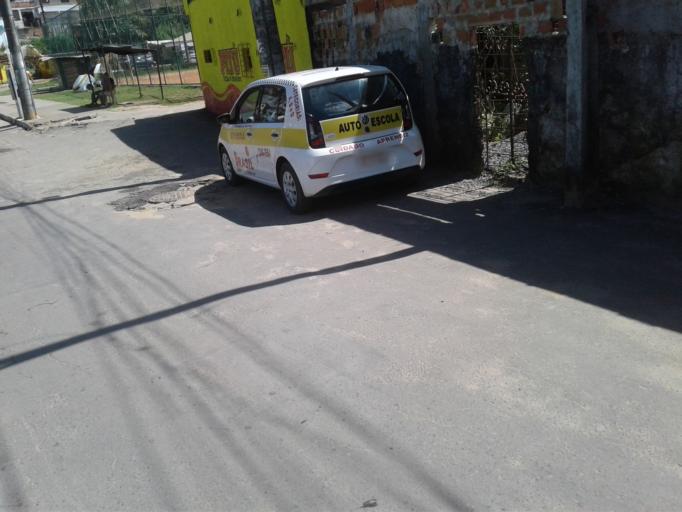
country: BR
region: Bahia
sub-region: Salvador
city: Salvador
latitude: -12.9124
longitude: -38.4730
